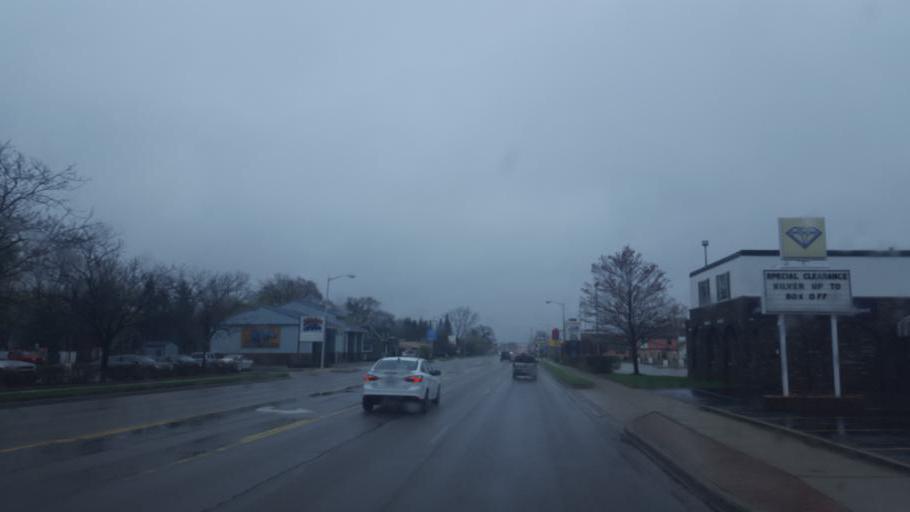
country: US
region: Michigan
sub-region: Isabella County
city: Mount Pleasant
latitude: 43.6018
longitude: -84.7678
